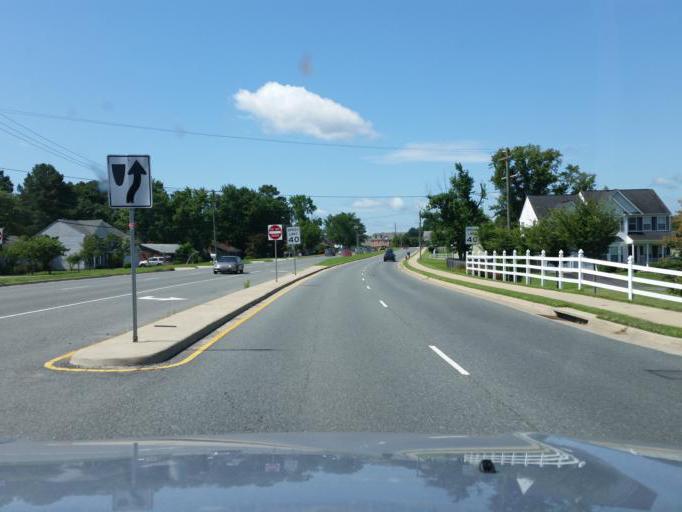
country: US
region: Virginia
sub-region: Stafford County
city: Falmouth
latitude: 38.3002
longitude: -77.5179
